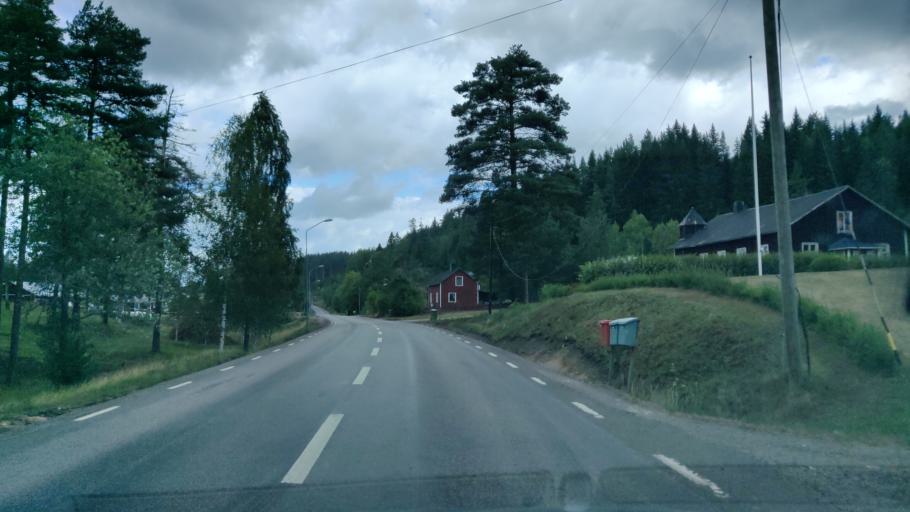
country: SE
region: Vaermland
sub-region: Torsby Kommun
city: Torsby
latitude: 60.6171
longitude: 13.0401
